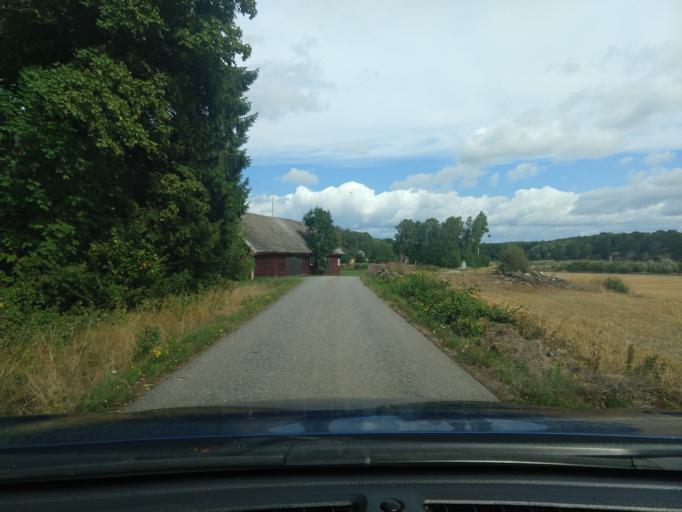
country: SE
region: Blekinge
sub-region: Ronneby Kommun
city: Brakne-Hoby
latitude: 56.2953
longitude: 15.1971
